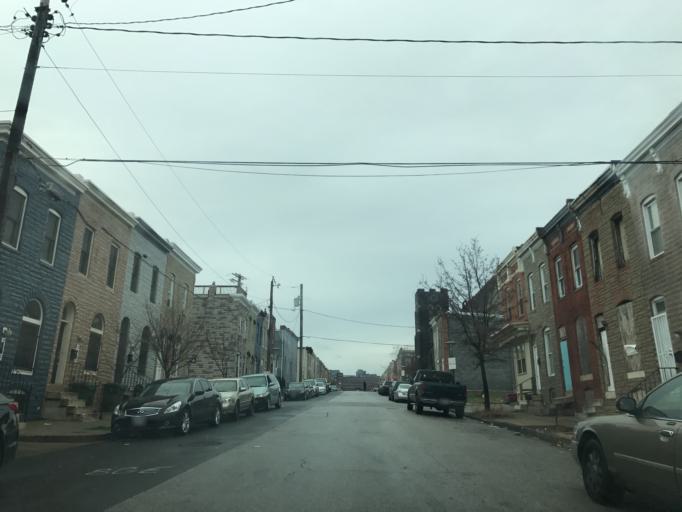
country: US
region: Maryland
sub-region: City of Baltimore
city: Baltimore
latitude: 39.2968
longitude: -76.5809
